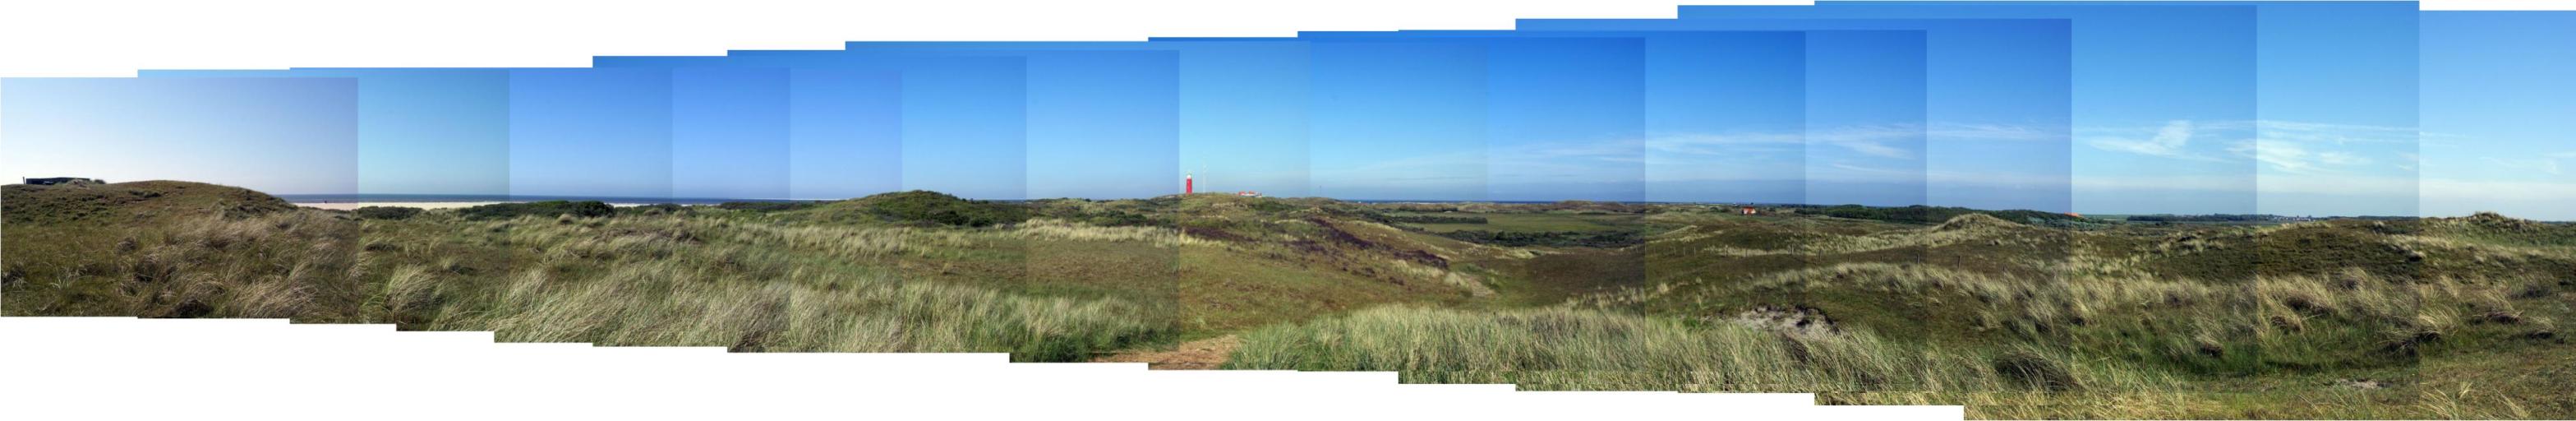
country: NL
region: North Holland
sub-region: Gemeente Texel
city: Den Burg
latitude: 53.1770
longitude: 4.8452
